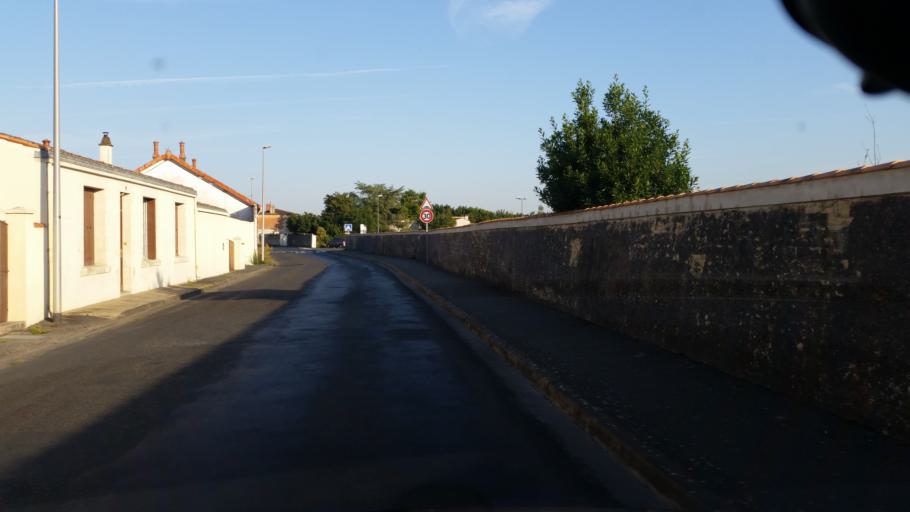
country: FR
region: Poitou-Charentes
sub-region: Departement de la Charente-Maritime
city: Marans
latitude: 46.3068
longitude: -0.9956
